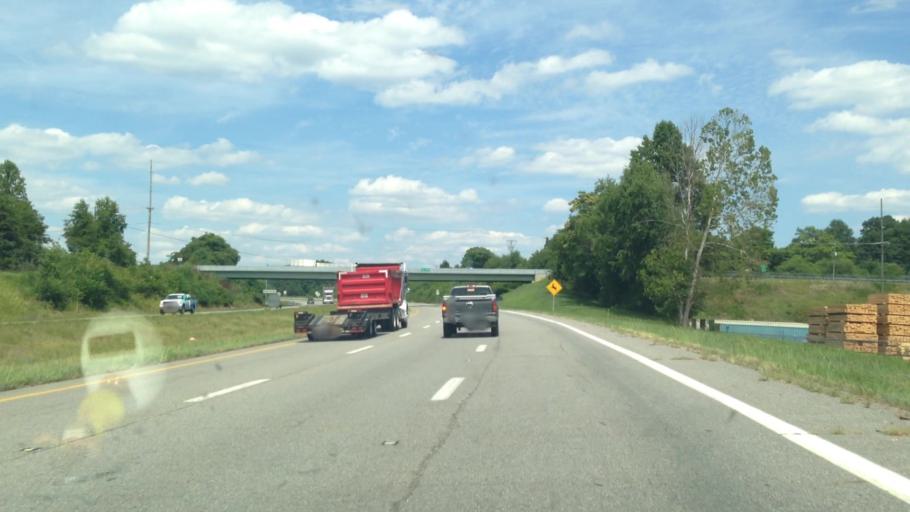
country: US
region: Virginia
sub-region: Henry County
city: Chatmoss
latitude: 36.6230
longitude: -79.8541
